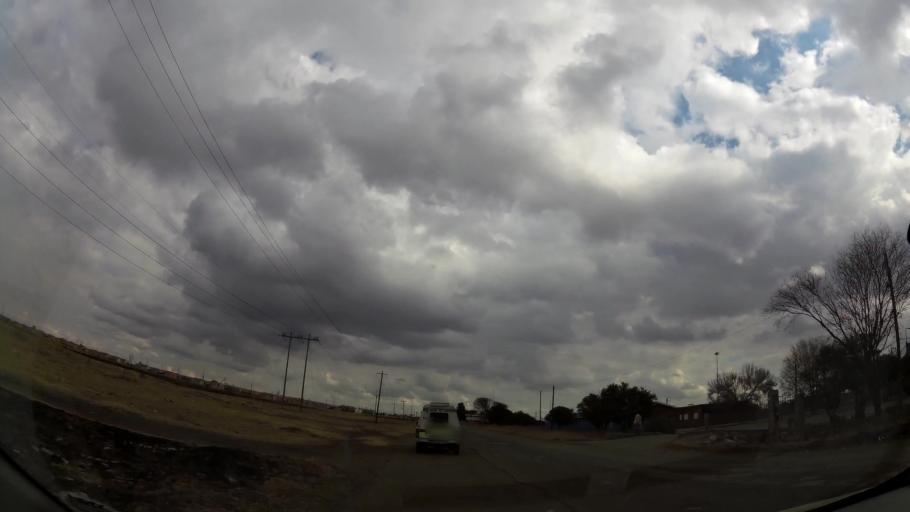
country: ZA
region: Orange Free State
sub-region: Fezile Dabi District Municipality
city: Sasolburg
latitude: -26.8545
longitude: 27.8673
